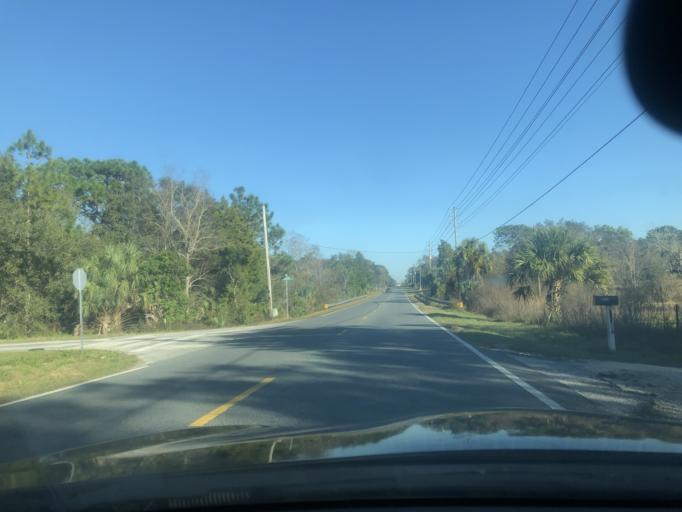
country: US
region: Florida
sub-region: Citrus County
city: Sugarmill Woods
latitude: 28.7640
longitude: -82.5409
